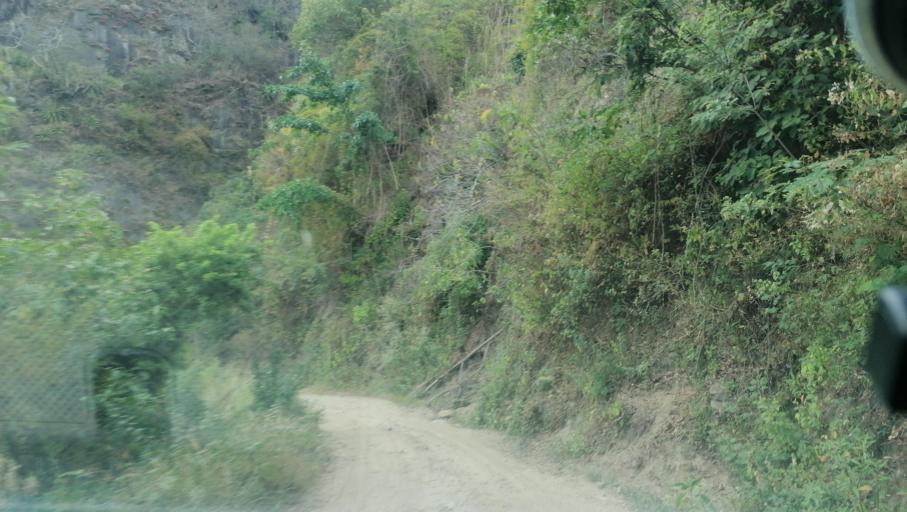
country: MX
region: Chiapas
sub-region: Cacahoatan
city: Benito Juarez
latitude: 15.1455
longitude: -92.1864
